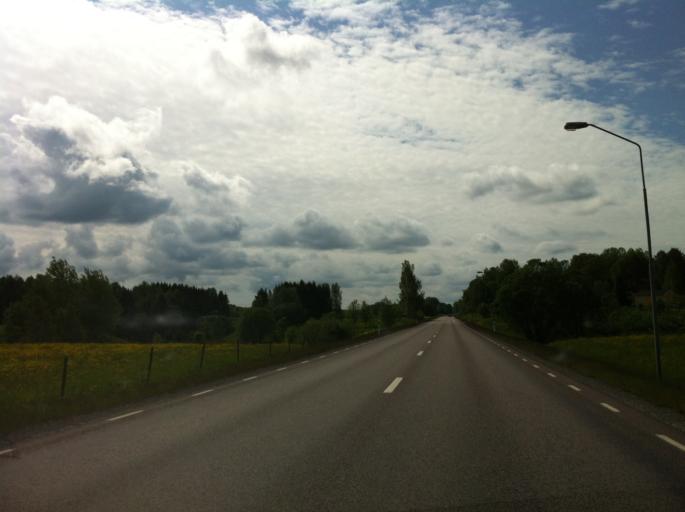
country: SE
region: Vaermland
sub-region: Karlstads Kommun
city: Edsvalla
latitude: 59.4786
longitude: 13.2161
